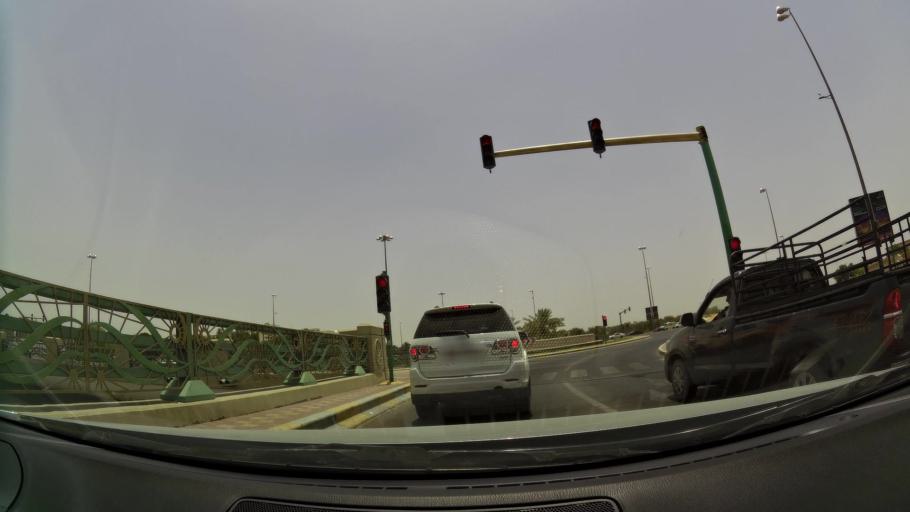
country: AE
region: Abu Dhabi
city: Al Ain
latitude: 24.2059
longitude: 55.7814
